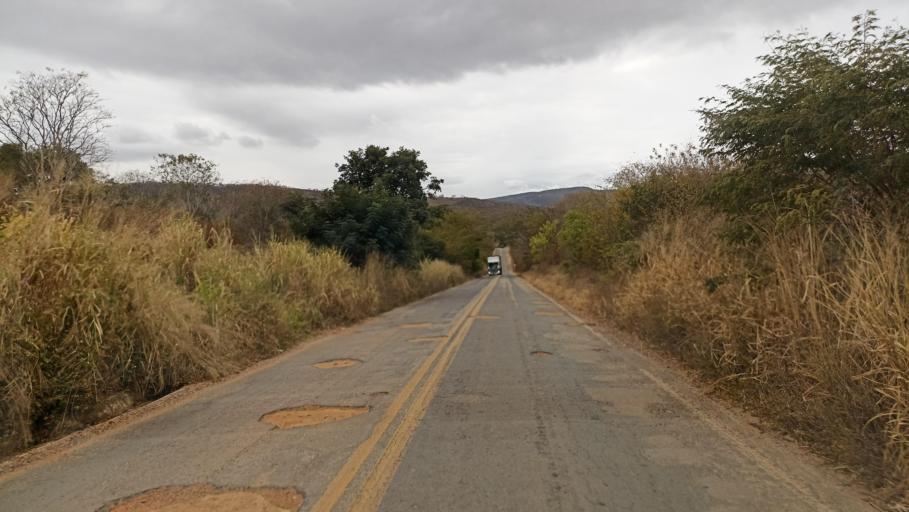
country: BR
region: Minas Gerais
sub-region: Itinga
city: Itinga
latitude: -16.6525
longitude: -41.8307
